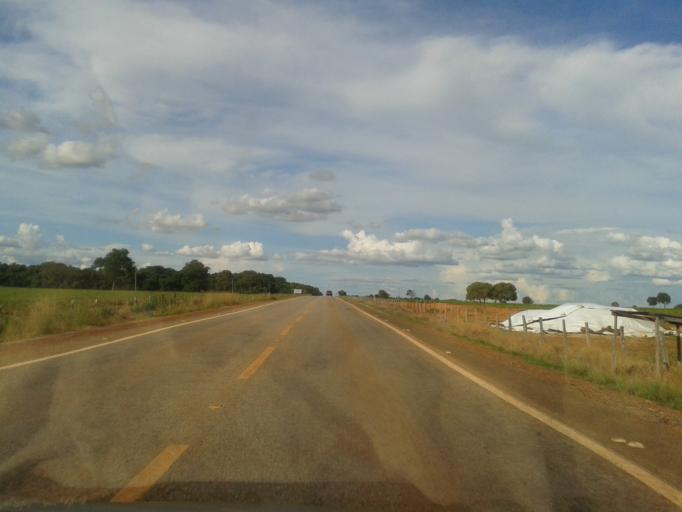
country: BR
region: Goias
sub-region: Mozarlandia
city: Mozarlandia
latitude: -14.3359
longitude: -50.4163
